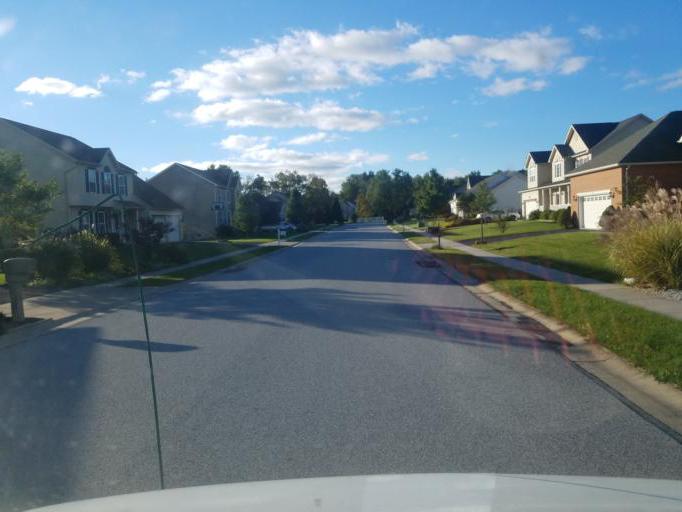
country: US
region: Pennsylvania
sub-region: Adams County
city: Gettysburg
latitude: 39.8647
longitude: -77.2436
